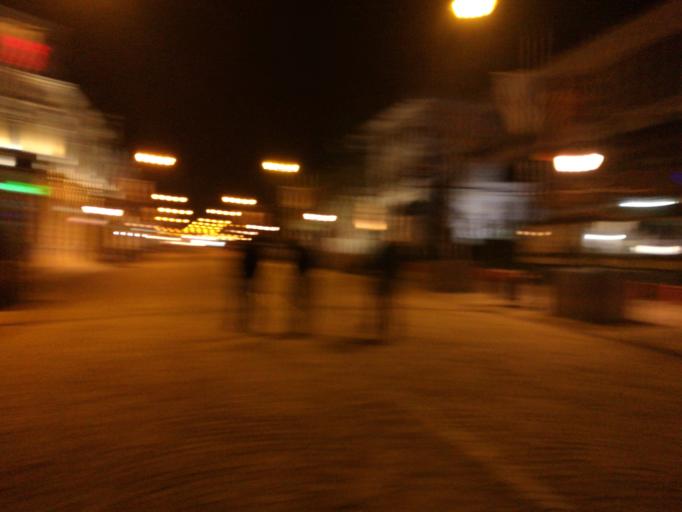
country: RO
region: Iasi
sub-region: Municipiul Iasi
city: Iasi
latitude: 47.1599
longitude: 27.5847
